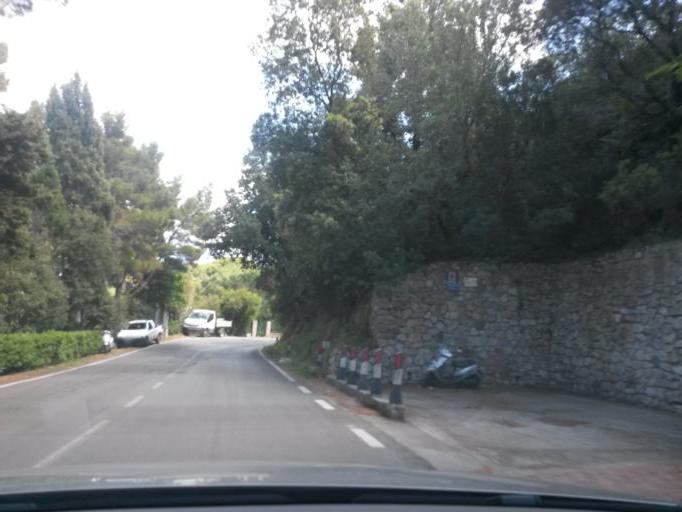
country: IT
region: Tuscany
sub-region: Provincia di Livorno
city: Marciana Marina
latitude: 42.7926
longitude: 10.2195
